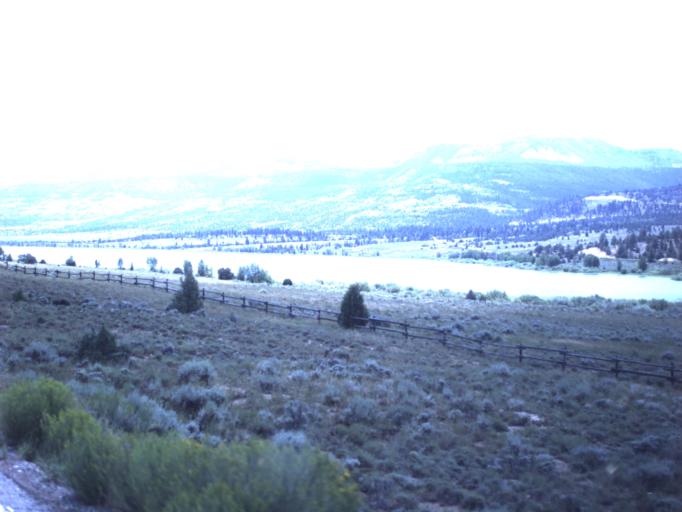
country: US
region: Utah
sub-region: Emery County
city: Orangeville
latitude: 39.3174
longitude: -111.2764
